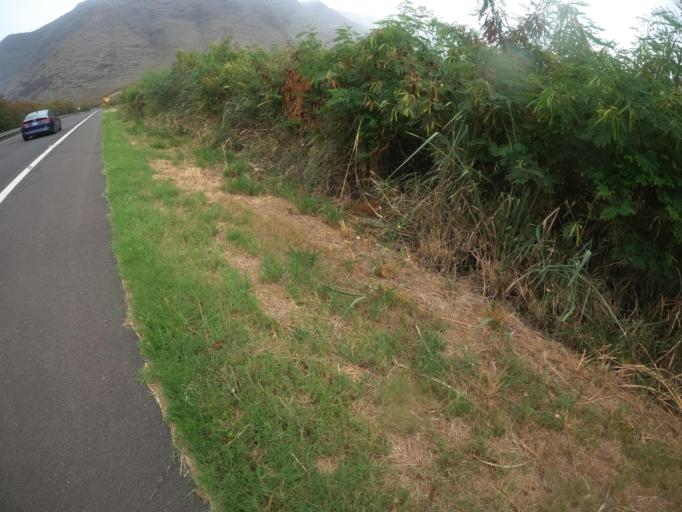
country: US
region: Hawaii
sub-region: Honolulu County
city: Makaha Valley
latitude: 21.5315
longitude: -158.2279
